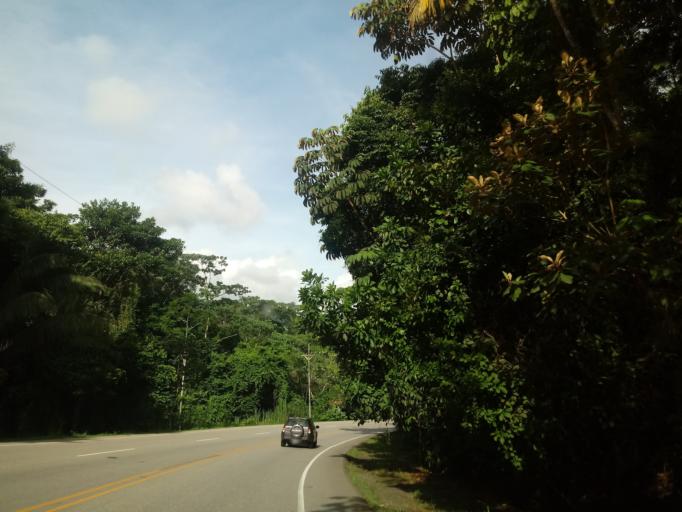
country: CR
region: San Jose
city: Daniel Flores
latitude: 9.2003
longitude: -83.7857
